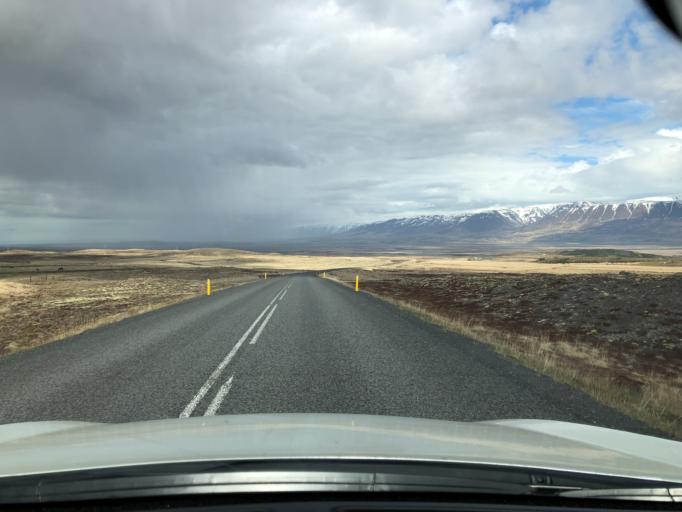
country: IS
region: Northwest
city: Saudarkrokur
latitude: 65.5335
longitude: -19.5121
